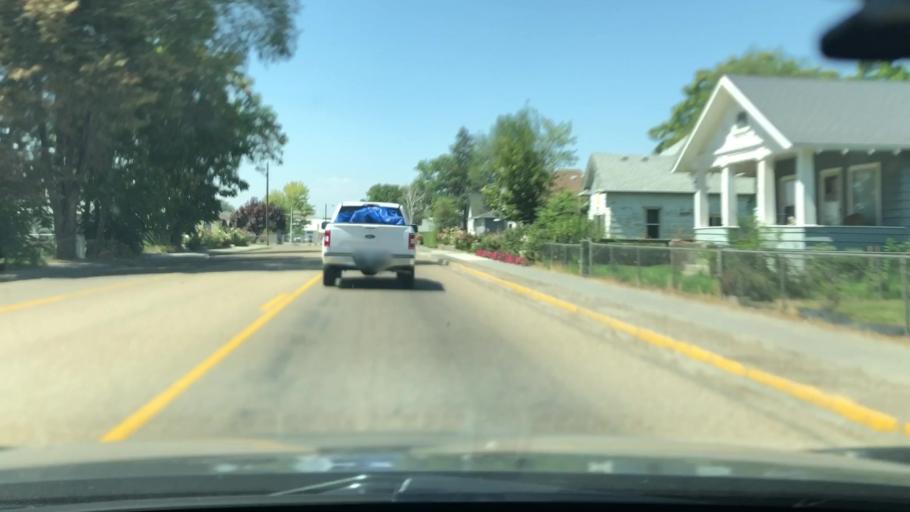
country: US
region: Idaho
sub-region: Canyon County
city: Parma
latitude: 43.7832
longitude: -116.9398
